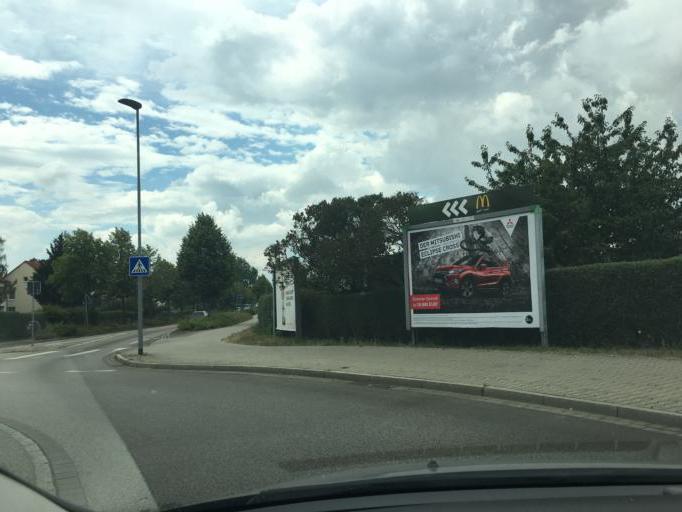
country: DE
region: Saxony-Anhalt
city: Merseburg
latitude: 51.3727
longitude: 11.9889
